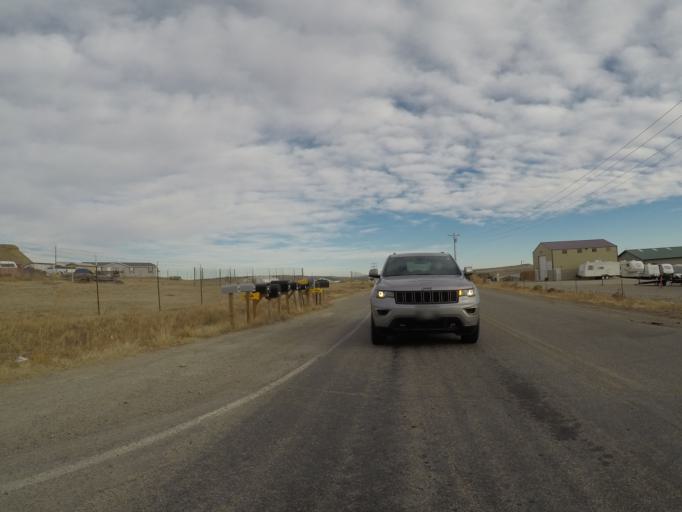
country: US
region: Montana
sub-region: Yellowstone County
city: Laurel
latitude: 45.7814
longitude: -108.7410
